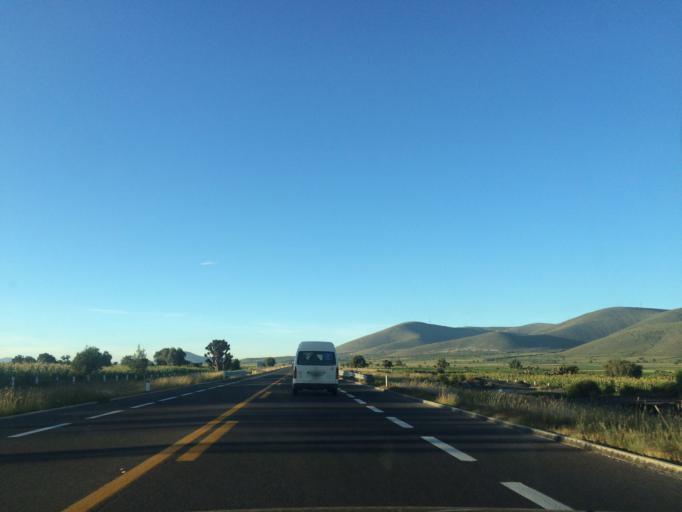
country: MX
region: Puebla
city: Cuacnopalan
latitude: 18.7595
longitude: -97.4822
